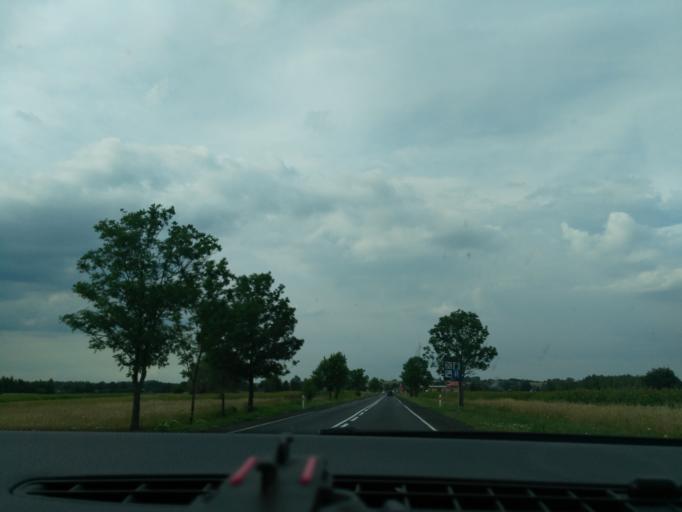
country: PL
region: Subcarpathian Voivodeship
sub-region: Powiat nizanski
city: Jezowe
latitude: 50.3639
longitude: 22.1240
